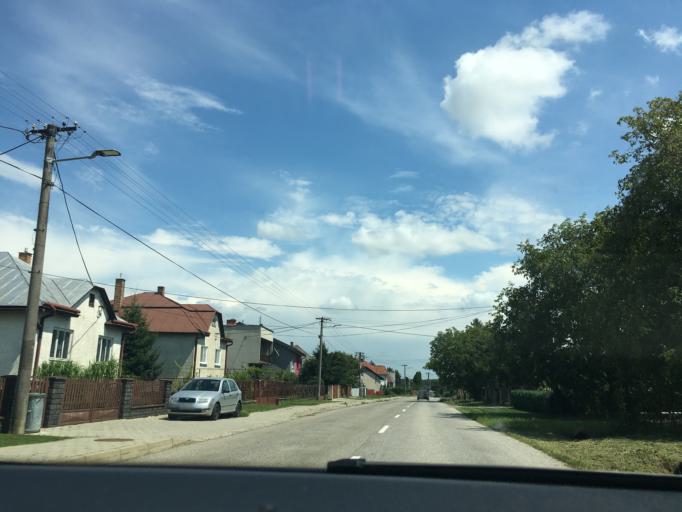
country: SK
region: Presovsky
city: Vranov nad Topl'ou
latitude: 48.8240
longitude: 21.6947
